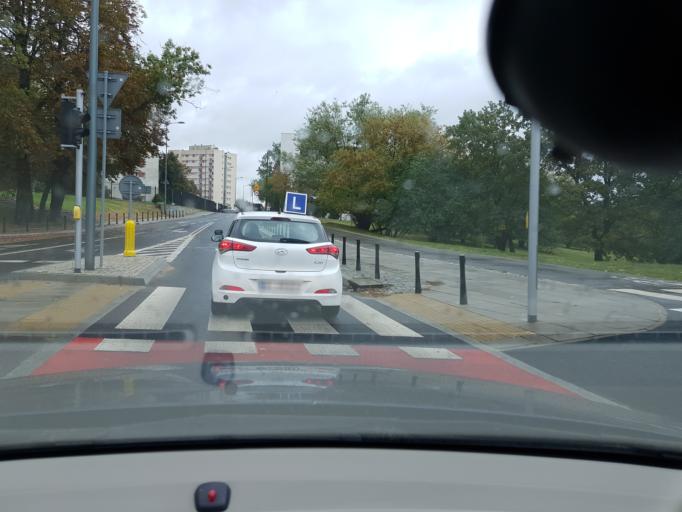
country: PL
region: Masovian Voivodeship
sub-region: Warszawa
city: Zoliborz
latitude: 52.2779
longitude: 20.9616
